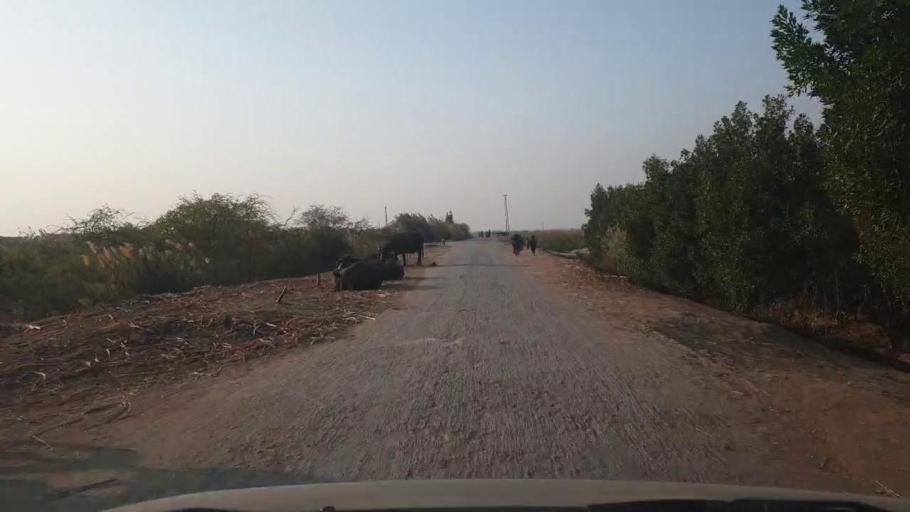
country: PK
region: Sindh
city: Mirwah Gorchani
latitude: 25.3726
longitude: 69.1267
